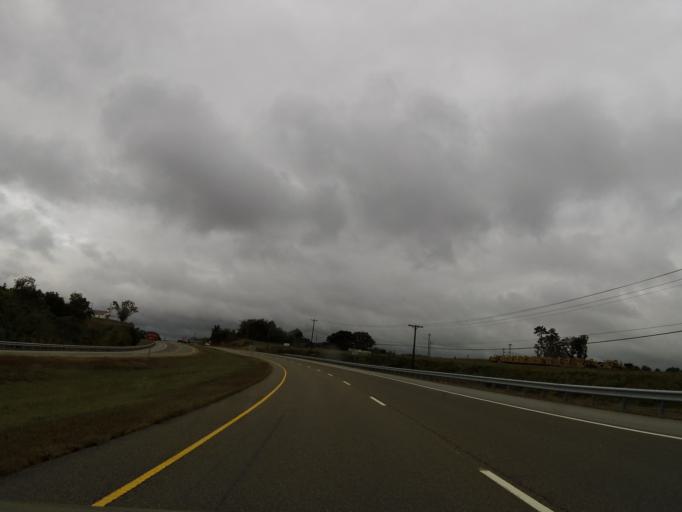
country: US
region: Tennessee
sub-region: Loudon County
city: Lenoir City
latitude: 35.7740
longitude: -84.2329
